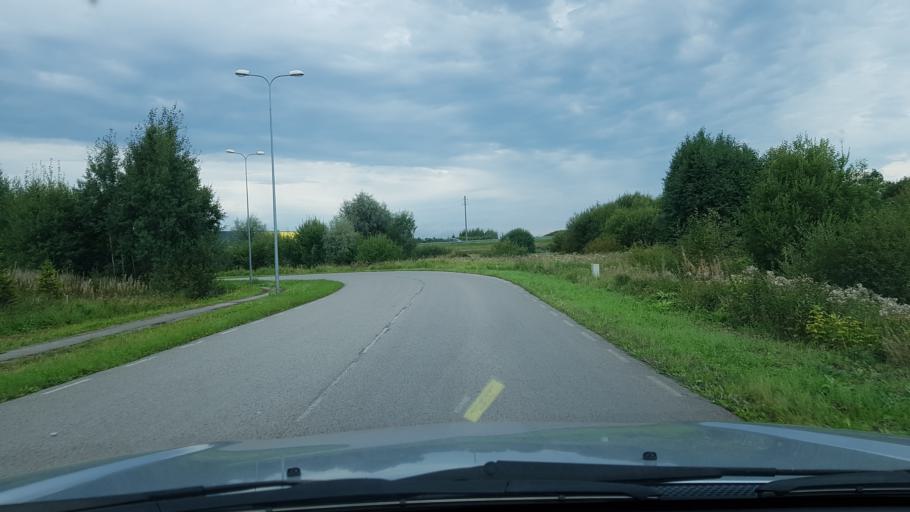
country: EE
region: Harju
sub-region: Rae vald
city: Jueri
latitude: 59.3470
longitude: 24.8968
